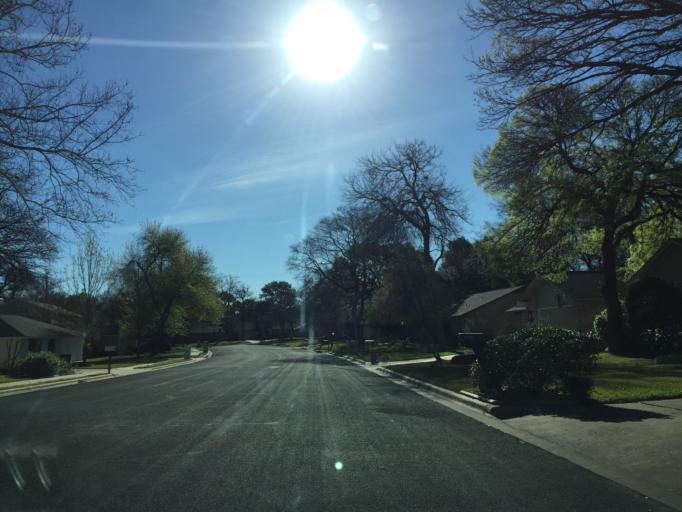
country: US
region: Texas
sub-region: Williamson County
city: Jollyville
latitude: 30.4017
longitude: -97.7328
